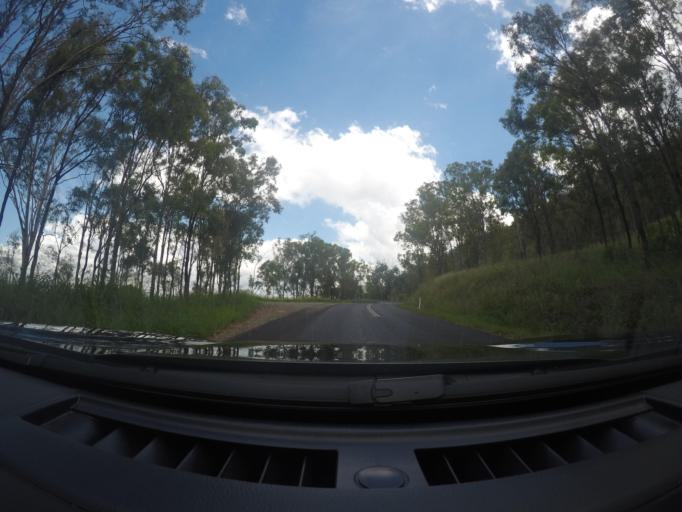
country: AU
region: Queensland
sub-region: Moreton Bay
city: Woodford
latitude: -27.0905
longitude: 152.5629
